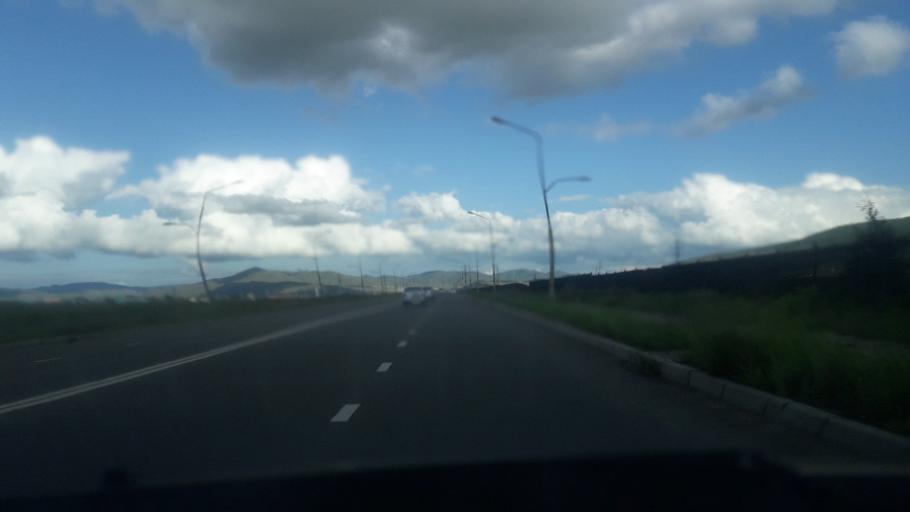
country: MN
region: Ulaanbaatar
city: Ulaanbaatar
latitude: 47.9007
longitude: 106.9899
